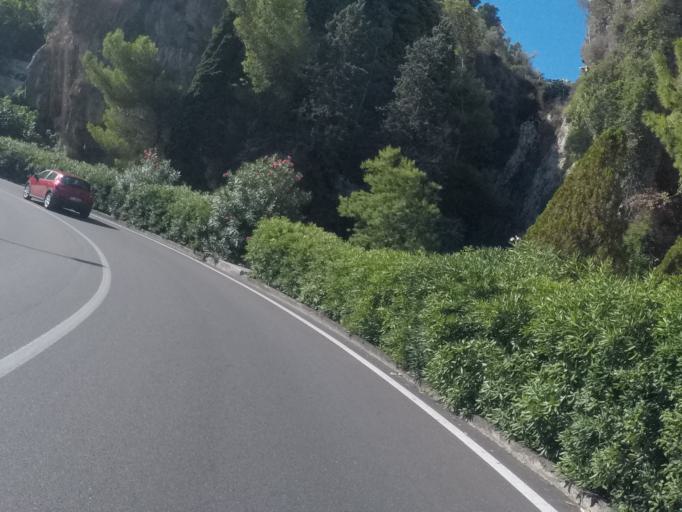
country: IT
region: Sicily
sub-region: Messina
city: Taormina
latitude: 37.8581
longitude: 15.2895
